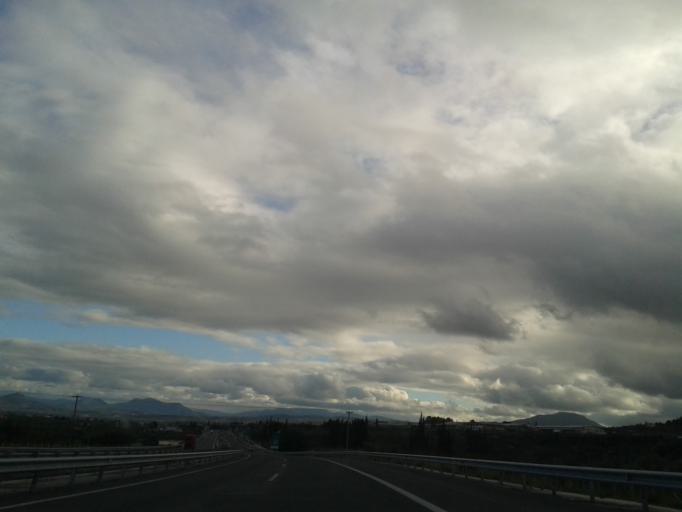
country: GR
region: Peloponnese
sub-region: Nomos Korinthias
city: Sikyon
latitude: 37.9822
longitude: 22.7360
